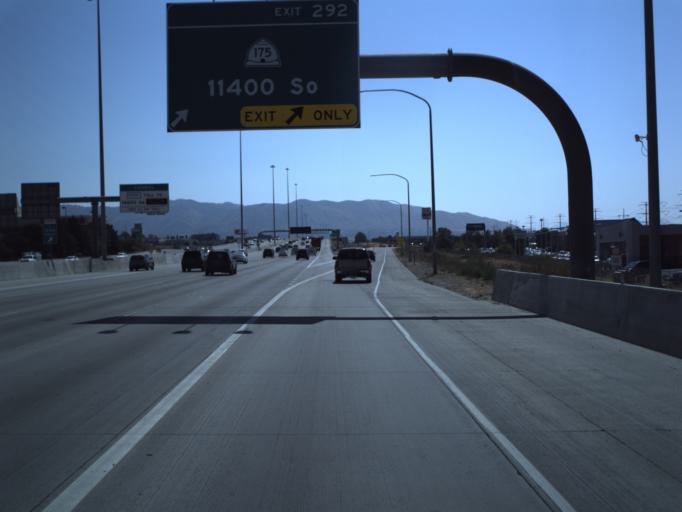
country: US
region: Utah
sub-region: Salt Lake County
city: South Jordan
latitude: 40.5504
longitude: -111.8965
